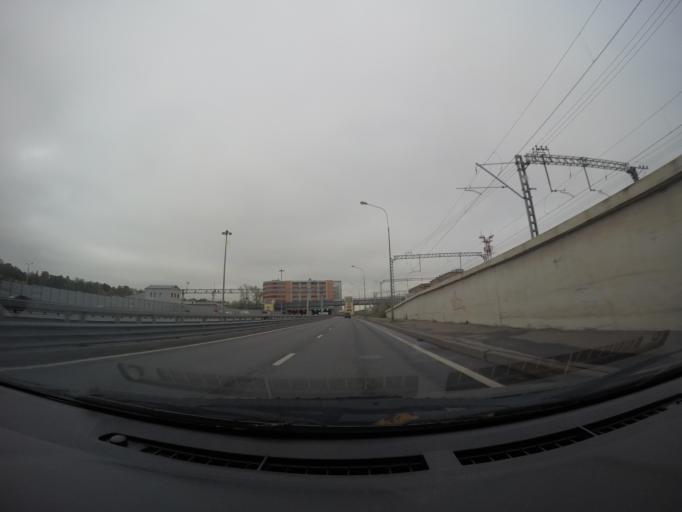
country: RU
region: Moskovskaya
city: Bogorodskoye
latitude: 55.7793
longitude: 37.7440
